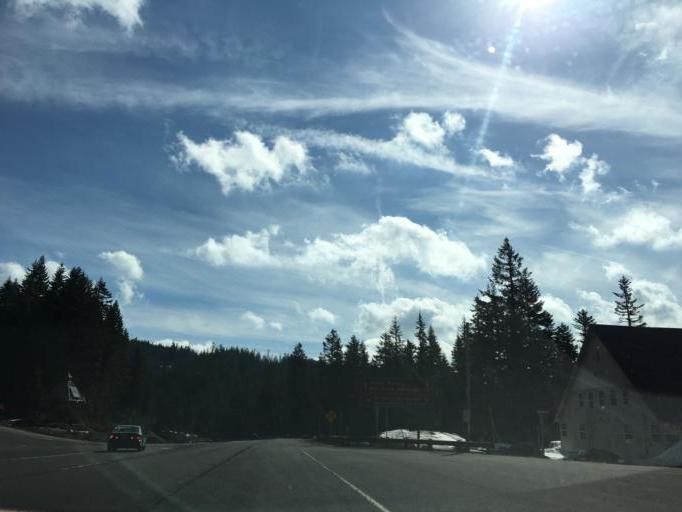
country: US
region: Oregon
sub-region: Clackamas County
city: Mount Hood Village
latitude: 45.3015
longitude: -121.7420
